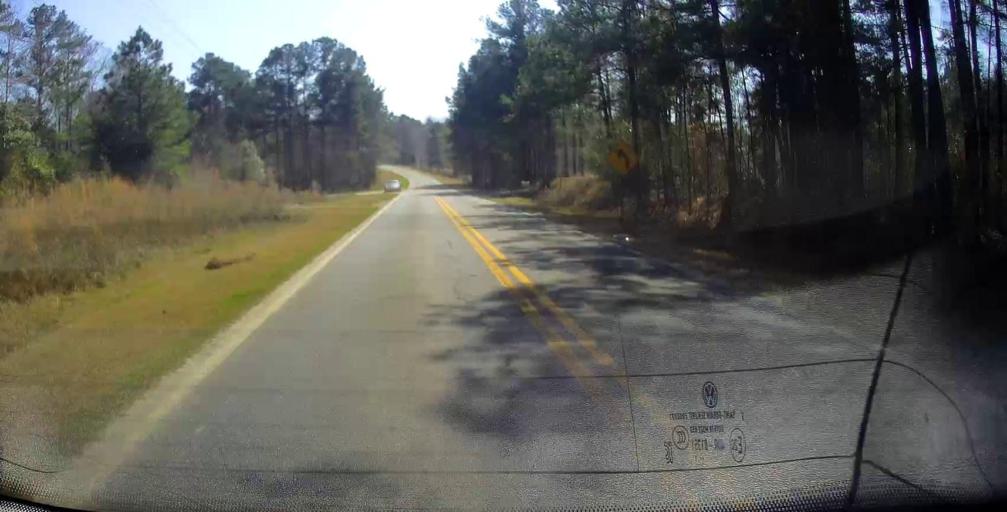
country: US
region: Georgia
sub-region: Jones County
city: Gray
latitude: 32.9348
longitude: -83.5357
